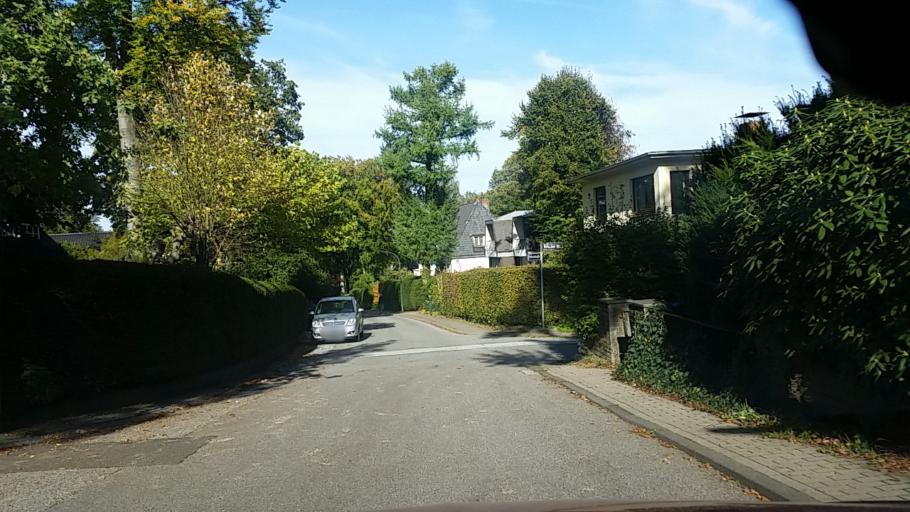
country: DE
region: Schleswig-Holstein
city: Halstenbek
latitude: 53.5680
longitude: 9.8043
